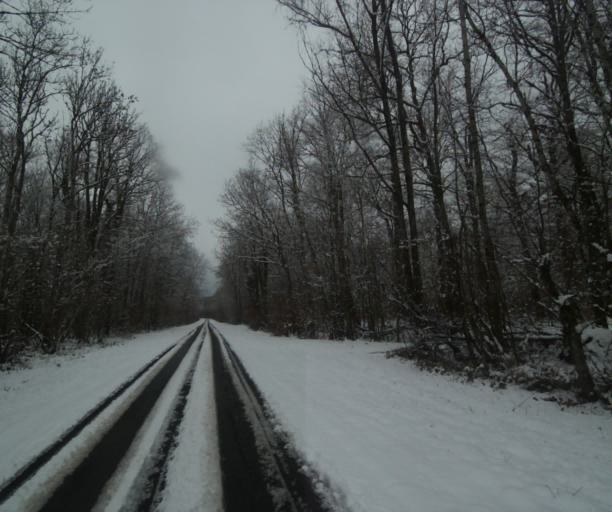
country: FR
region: Champagne-Ardenne
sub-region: Departement de la Haute-Marne
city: Wassy
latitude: 48.4661
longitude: 4.9472
